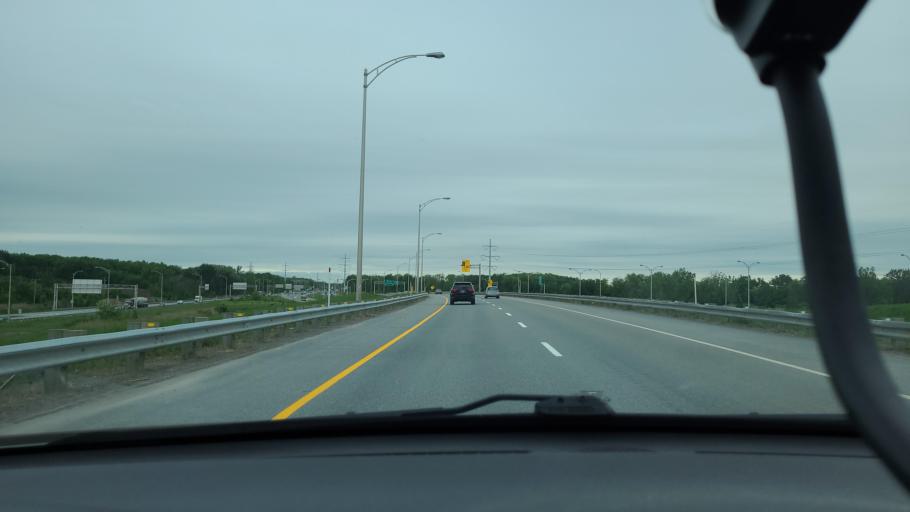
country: CA
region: Quebec
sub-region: Lanaudiere
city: Terrebonne
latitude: 45.6551
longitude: -73.6454
